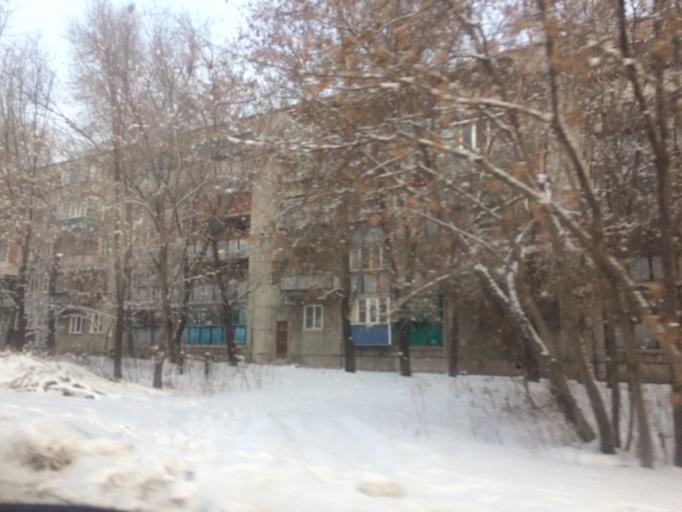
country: RU
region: Chelyabinsk
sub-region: Gorod Magnitogorsk
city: Magnitogorsk
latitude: 53.4690
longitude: 59.0751
